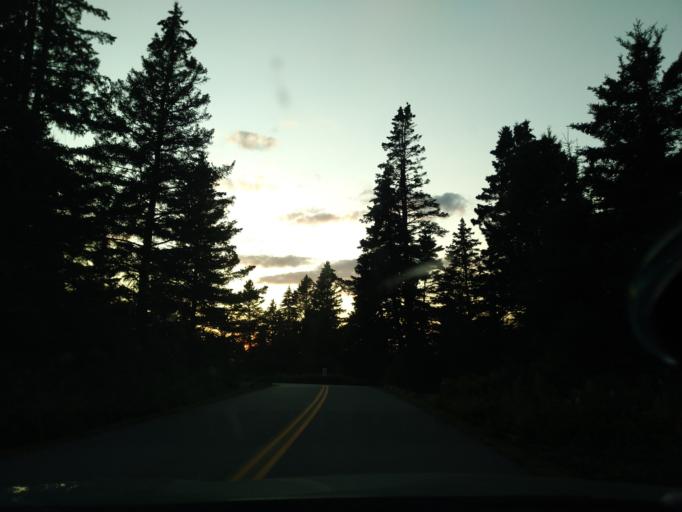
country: US
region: Maine
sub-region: Hancock County
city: Gouldsboro
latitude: 44.3747
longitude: -68.0741
